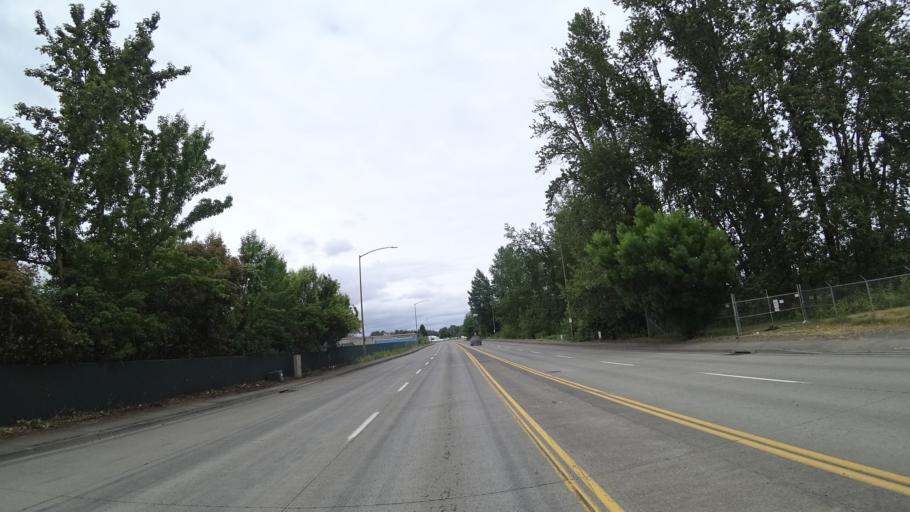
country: US
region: Washington
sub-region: Clark County
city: Vancouver
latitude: 45.6141
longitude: -122.7053
